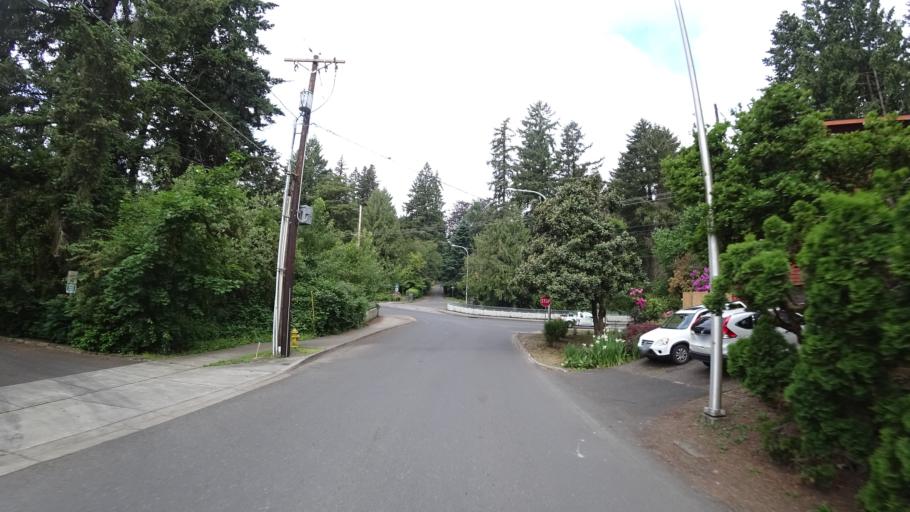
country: US
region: Oregon
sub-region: Washington County
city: Garden Home-Whitford
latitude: 45.4693
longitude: -122.7485
